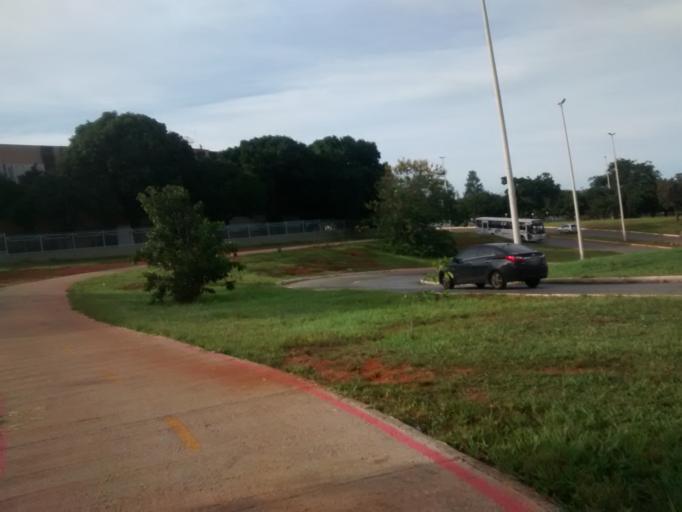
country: BR
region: Federal District
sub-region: Brasilia
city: Brasilia
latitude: -15.8016
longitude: -47.8768
